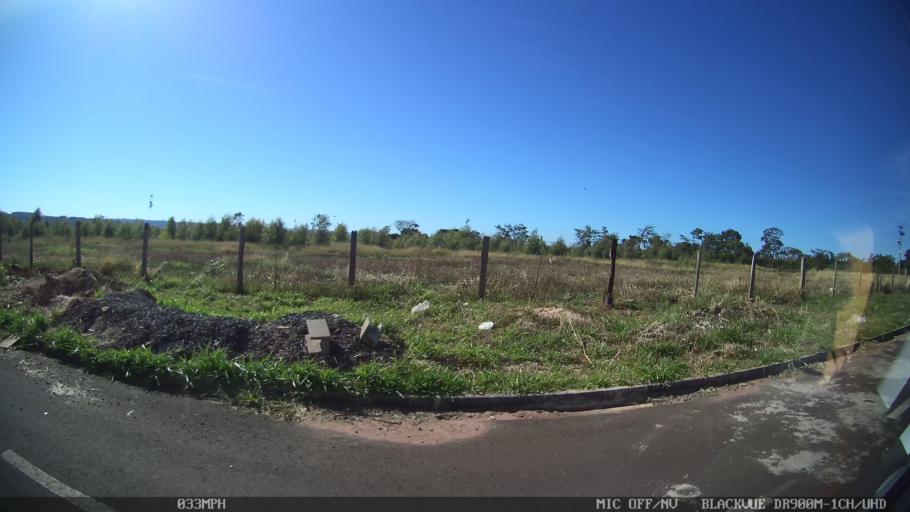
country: BR
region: Sao Paulo
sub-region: Franca
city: Franca
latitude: -20.5669
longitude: -47.3437
